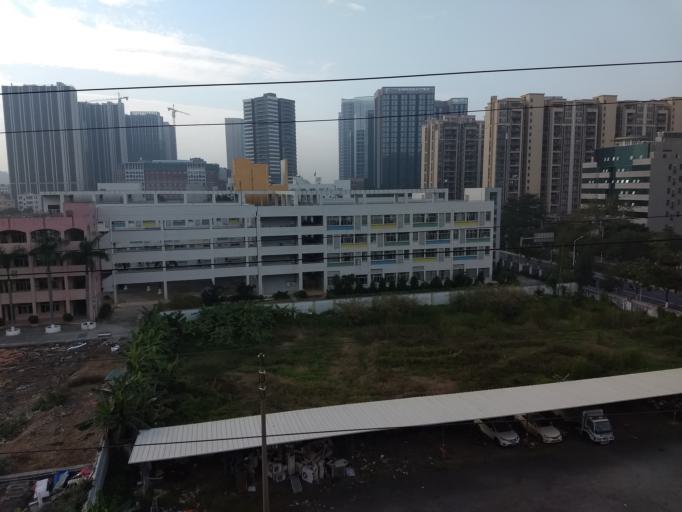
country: CN
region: Guangdong
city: Nansha
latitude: 22.8020
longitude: 113.5413
